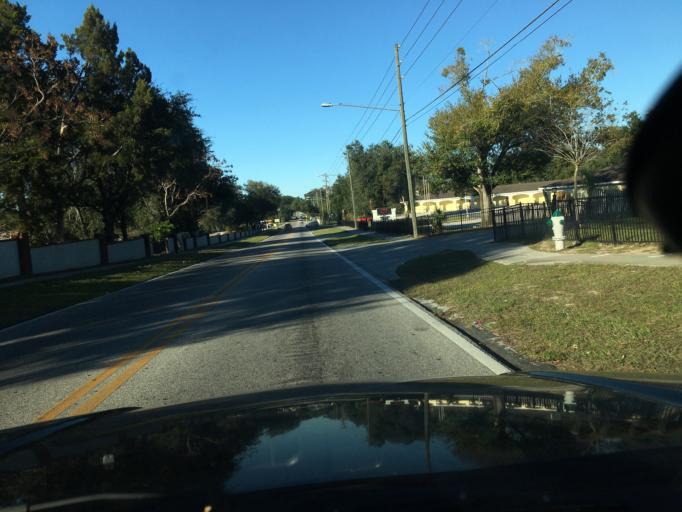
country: US
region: Florida
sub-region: Orange County
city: Lockhart
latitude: 28.5946
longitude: -81.4678
